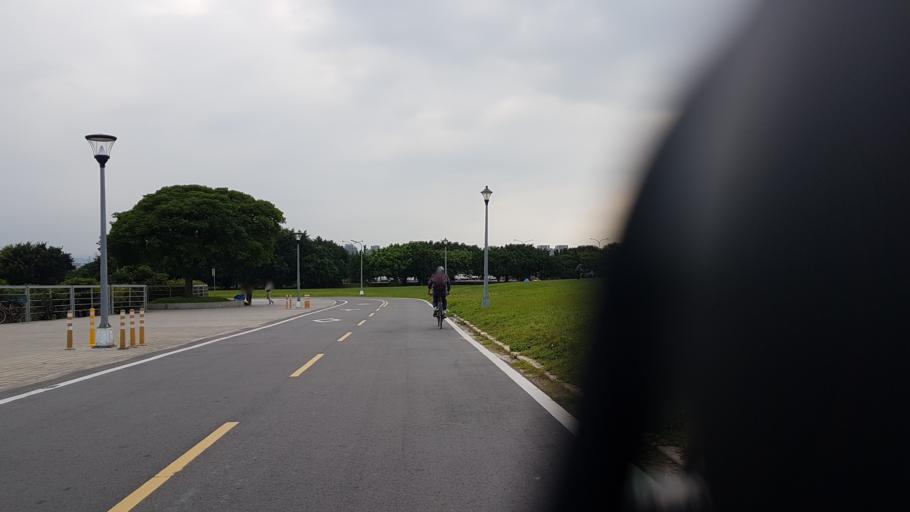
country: TW
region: Taipei
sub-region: Taipei
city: Banqiao
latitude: 25.0185
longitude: 121.5039
